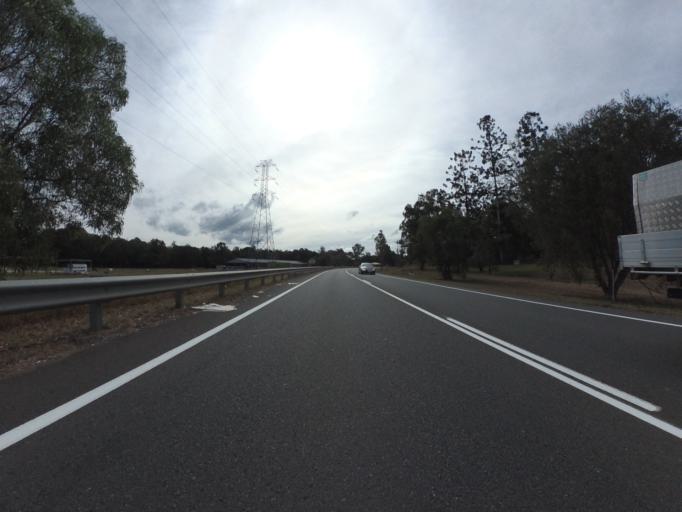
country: AU
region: Queensland
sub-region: Brisbane
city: Pullenvale
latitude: -27.5466
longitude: 152.8892
